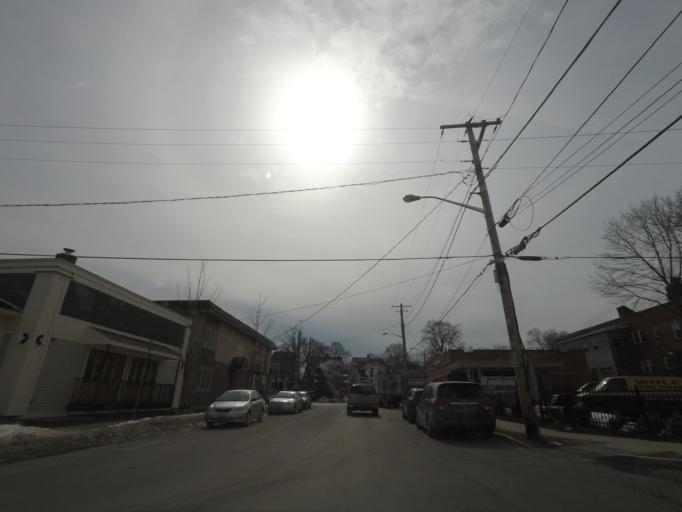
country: US
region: New York
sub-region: Albany County
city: West Albany
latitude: 42.6537
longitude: -73.7885
